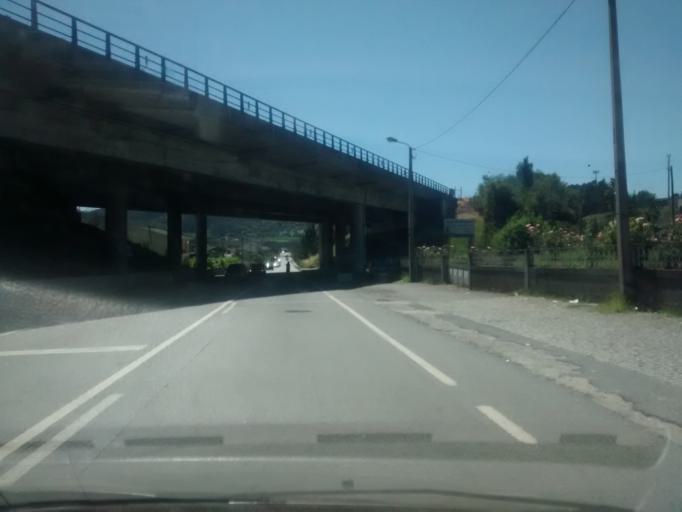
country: PT
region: Braga
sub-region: Braga
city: Oliveira
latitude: 41.5312
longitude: -8.4773
